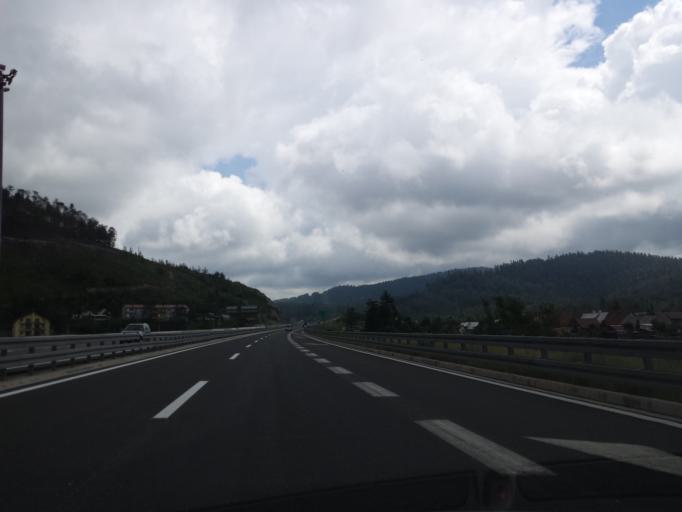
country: HR
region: Primorsko-Goranska
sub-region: Grad Delnice
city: Delnice
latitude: 45.3195
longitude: 14.7280
